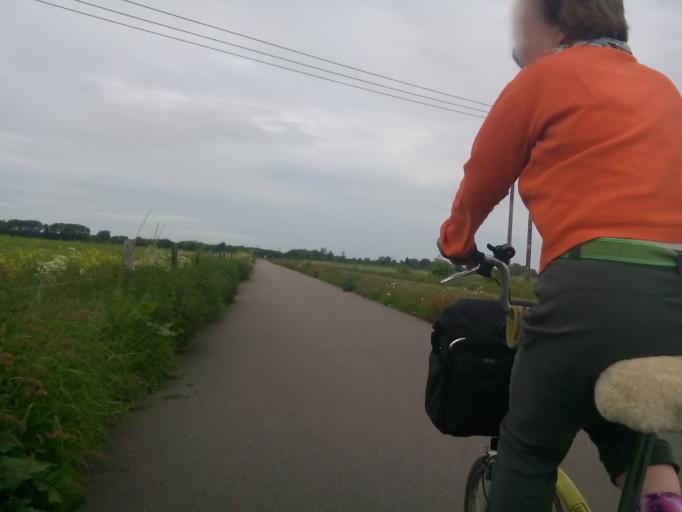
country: GB
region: England
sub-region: Cambridgeshire
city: Histon
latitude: 52.2550
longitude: 0.0900
